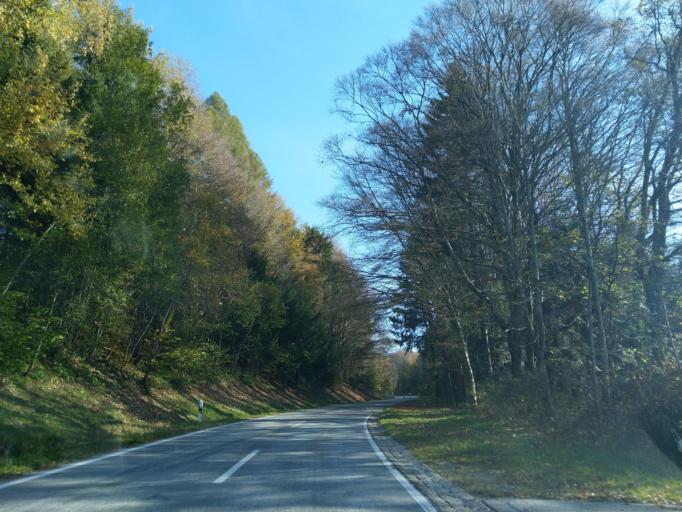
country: DE
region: Bavaria
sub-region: Lower Bavaria
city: Hunding
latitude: 48.8170
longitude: 13.1925
